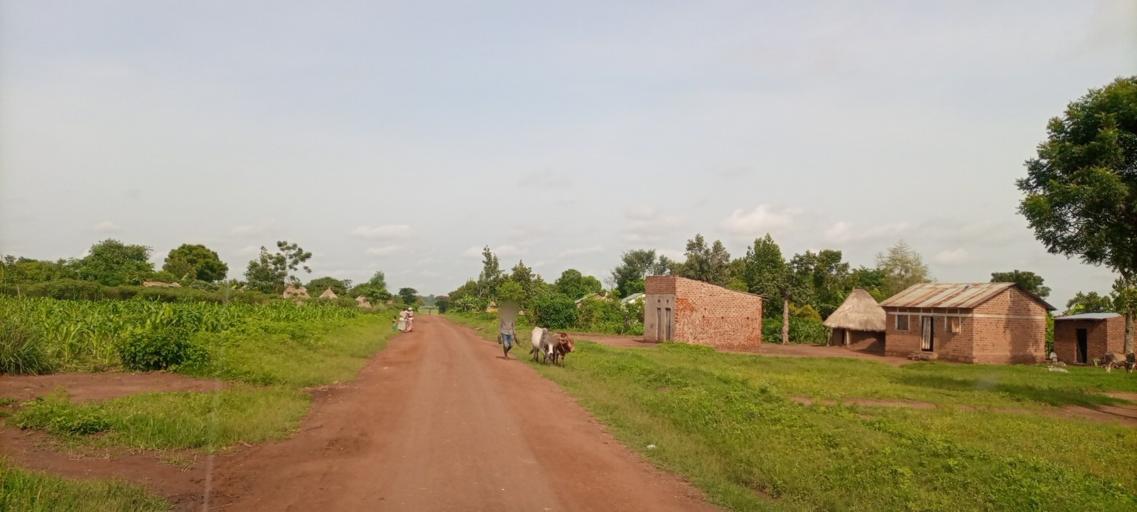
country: UG
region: Eastern Region
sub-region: Kibuku District
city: Kibuku
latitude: 1.1042
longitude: 33.7823
